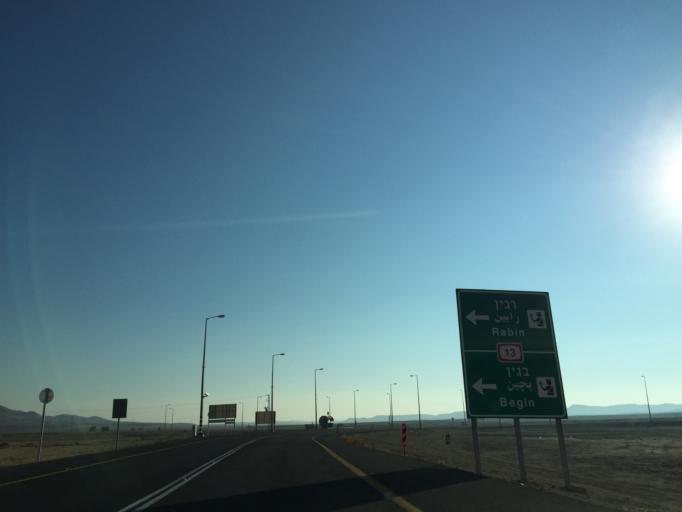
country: IL
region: Southern District
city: Mitzpe Ramon
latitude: 30.2777
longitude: 35.0186
